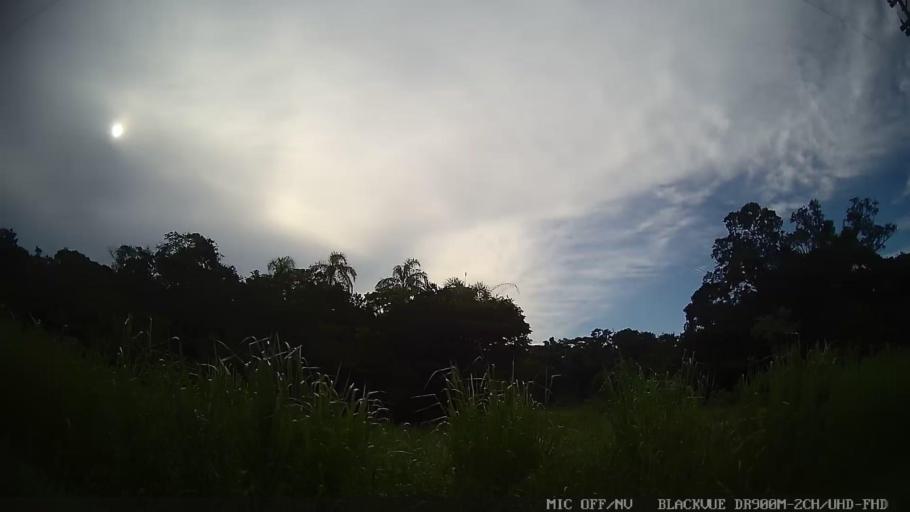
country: BR
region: Sao Paulo
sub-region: Iguape
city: Iguape
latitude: -24.6553
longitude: -47.4072
